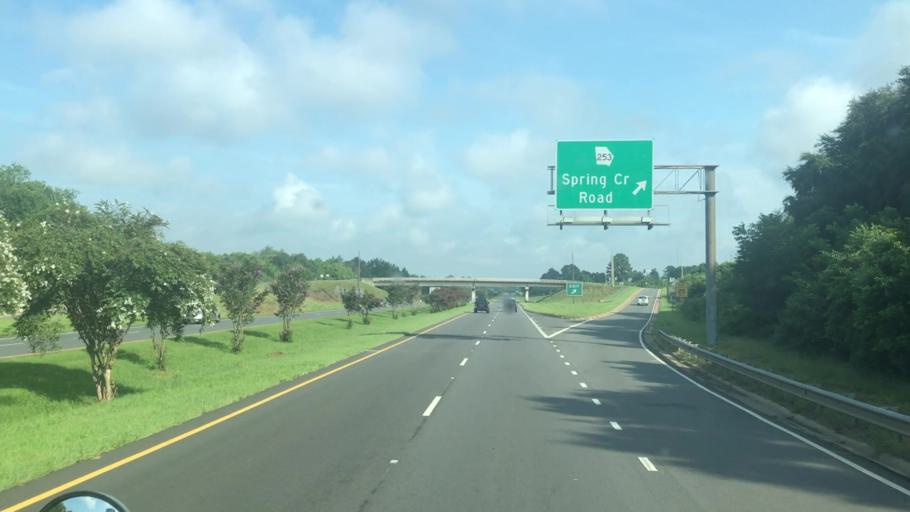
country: US
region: Georgia
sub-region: Decatur County
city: Bainbridge
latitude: 30.9096
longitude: -84.5921
